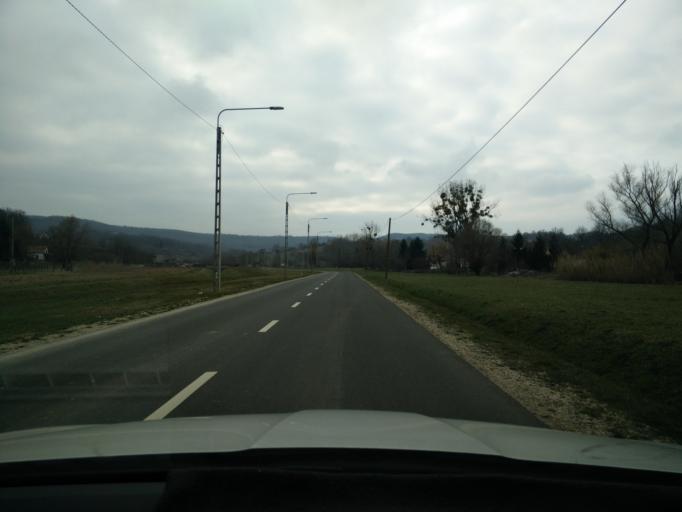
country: HU
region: Tolna
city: Szekszard
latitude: 46.3324
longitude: 18.6766
